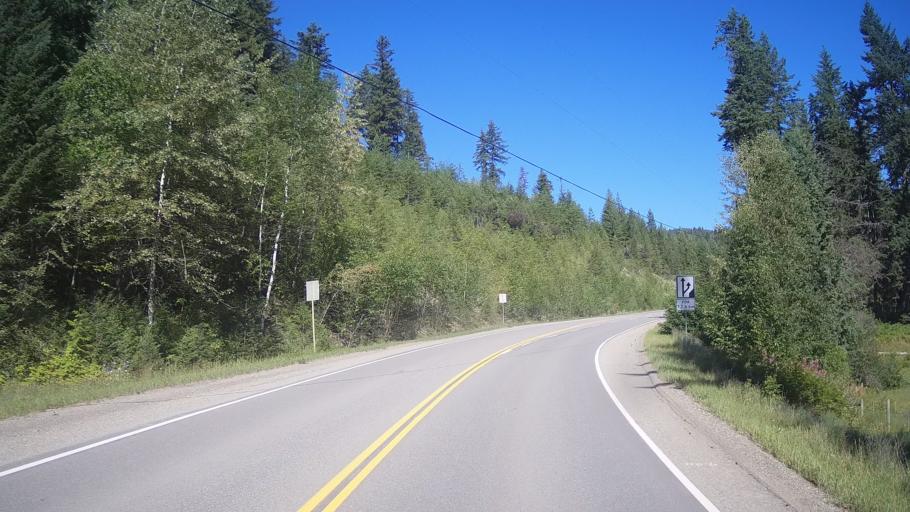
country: CA
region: British Columbia
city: Kamloops
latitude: 51.4538
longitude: -120.2229
